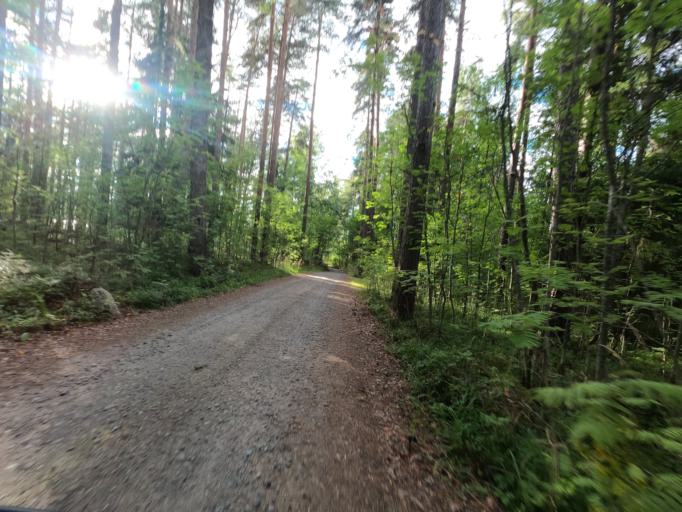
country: FI
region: North Karelia
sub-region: Joensuu
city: Joensuu
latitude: 62.6009
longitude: 29.7224
